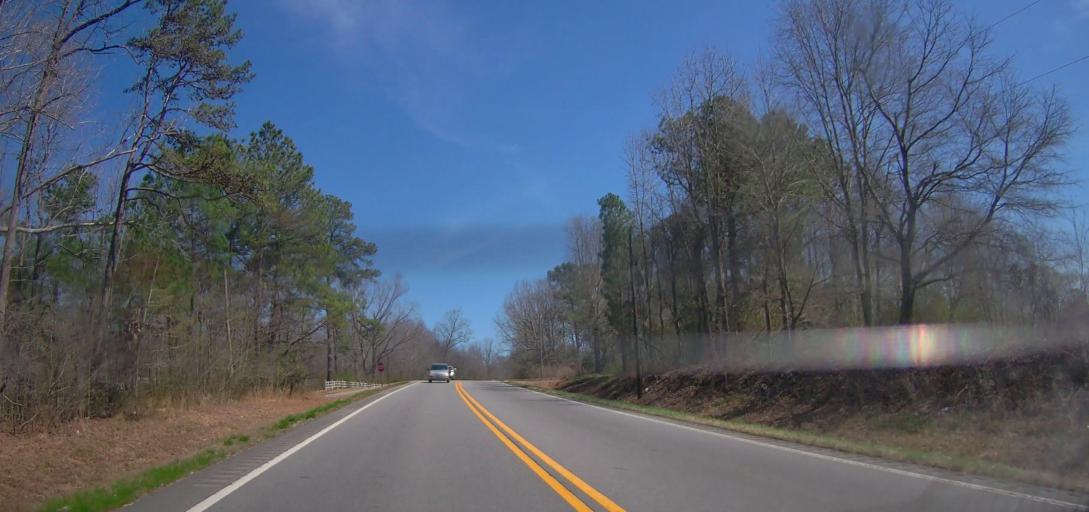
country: US
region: Alabama
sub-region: Blount County
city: Blountsville
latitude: 34.1735
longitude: -86.5338
